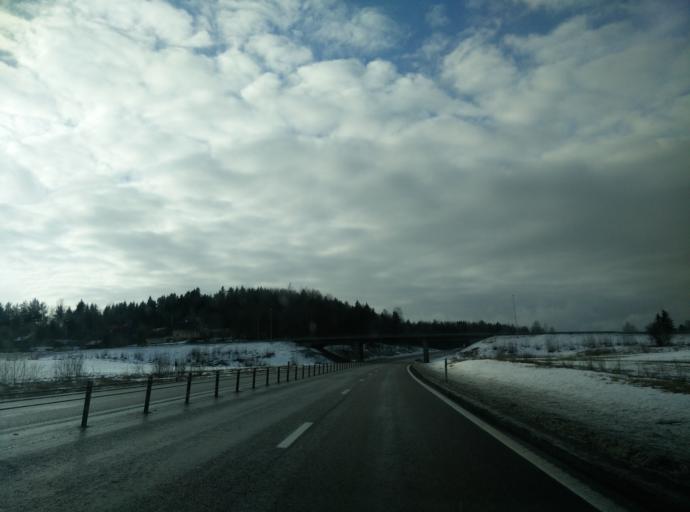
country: SE
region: Gaevleborg
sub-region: Sandvikens Kommun
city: Jarbo
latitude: 60.5745
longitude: 16.5340
